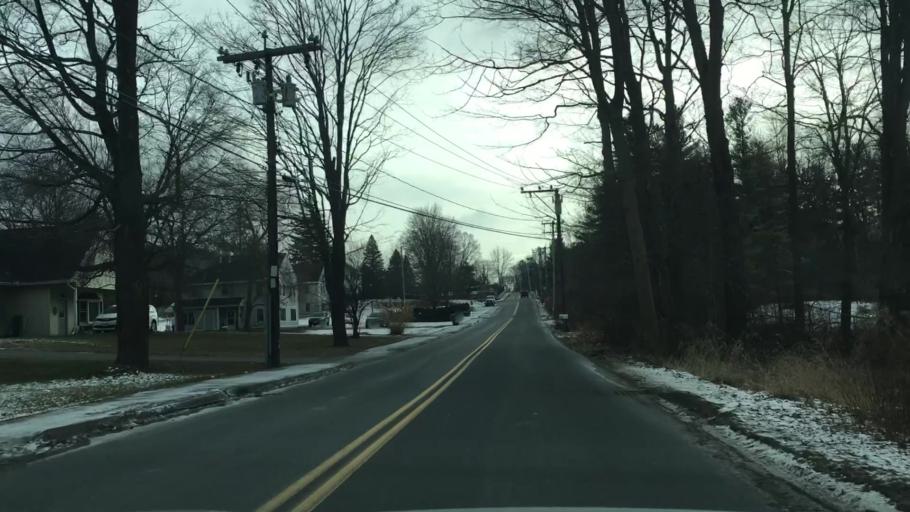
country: US
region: Massachusetts
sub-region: Berkshire County
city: Lee
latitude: 42.2991
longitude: -73.2497
